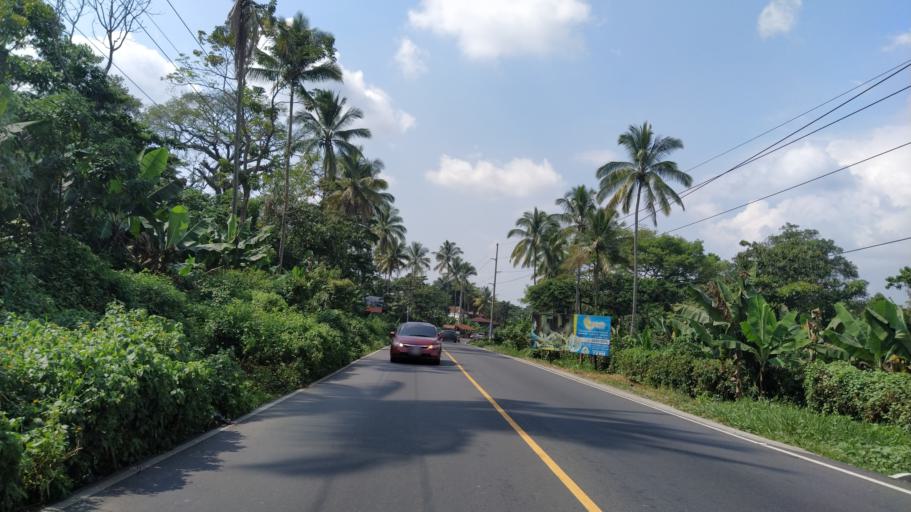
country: GT
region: Quetzaltenango
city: El Palmar
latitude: 14.6337
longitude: -91.5812
